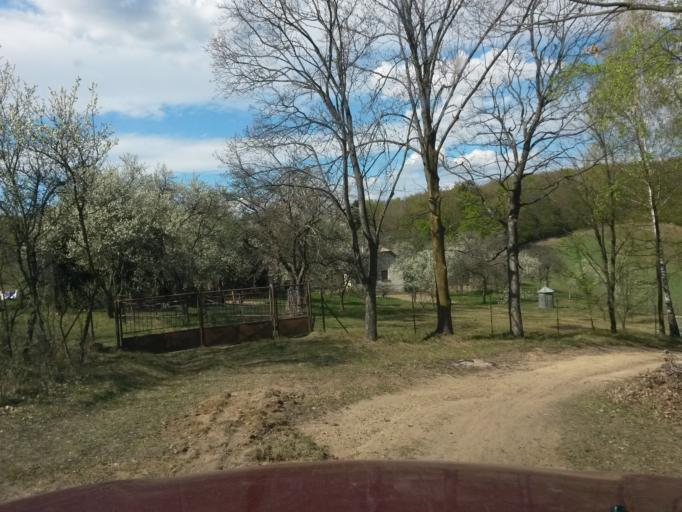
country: SK
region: Presovsky
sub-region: Okres Presov
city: Presov
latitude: 48.9387
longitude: 21.1213
